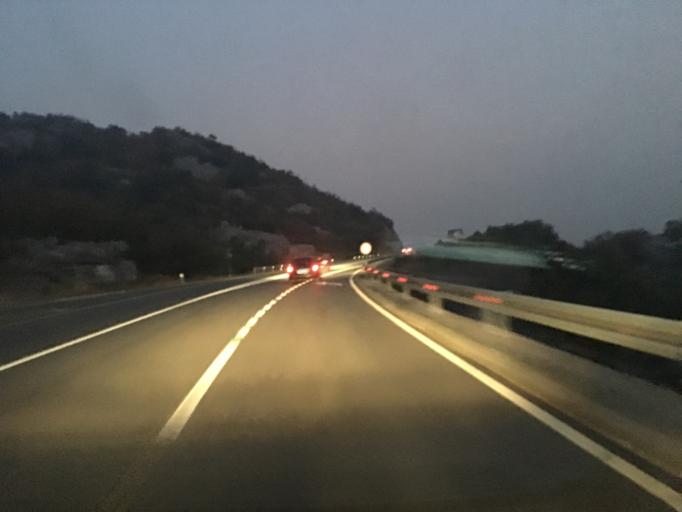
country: ME
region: Cetinje
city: Cetinje
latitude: 42.3811
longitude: 19.0178
